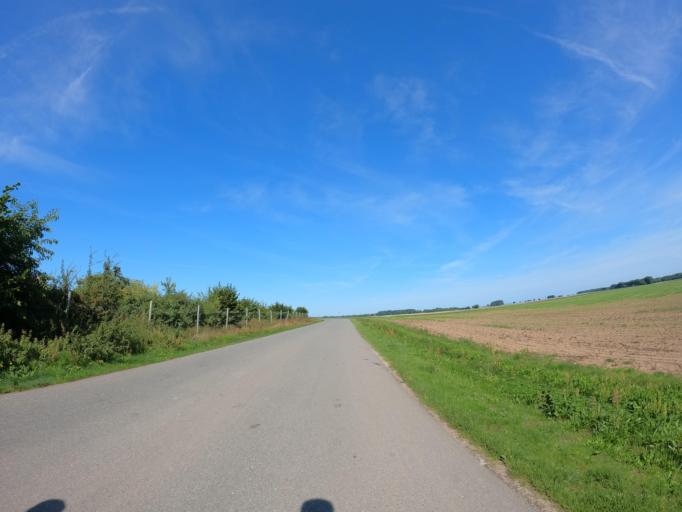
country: DE
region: Mecklenburg-Vorpommern
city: Kramerhof
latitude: 54.3525
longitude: 13.0481
